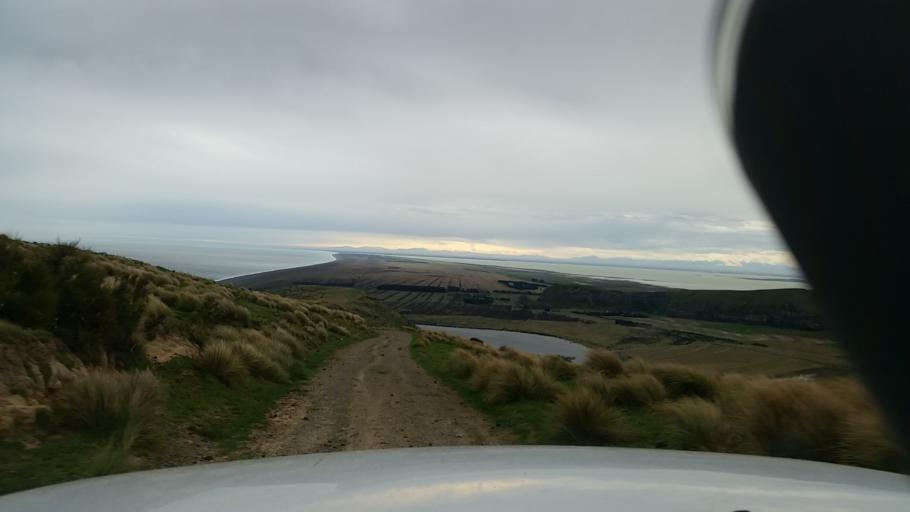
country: NZ
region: Canterbury
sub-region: Christchurch City
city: Christchurch
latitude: -43.8180
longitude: 172.7376
